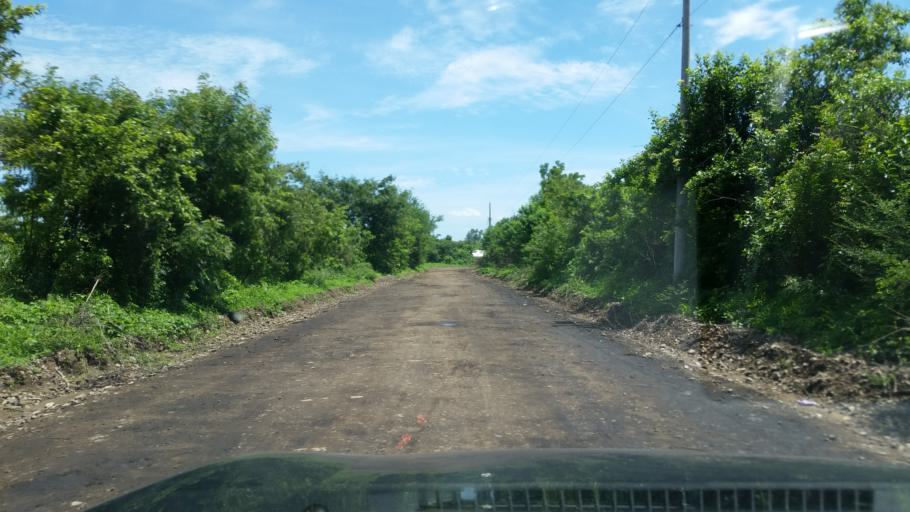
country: NI
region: Chinandega
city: Puerto Morazan
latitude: 12.7616
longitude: -87.1236
